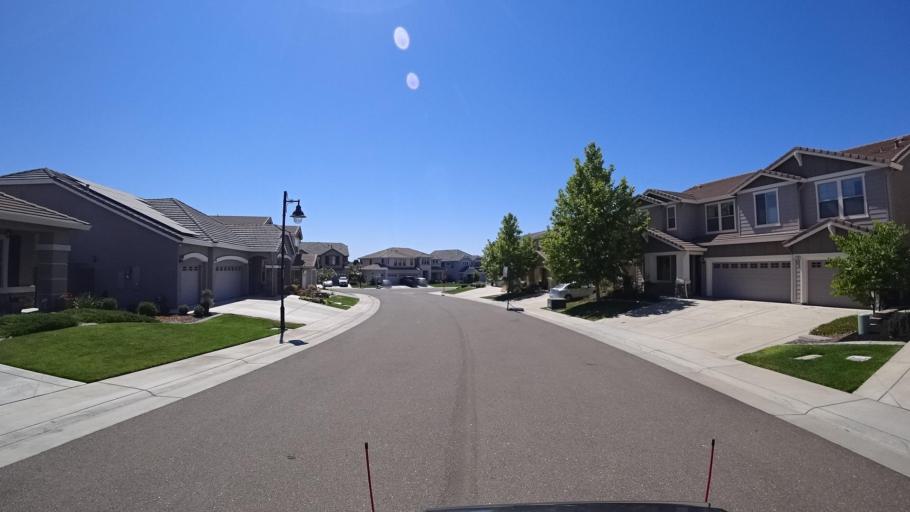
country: US
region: California
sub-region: Placer County
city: Rocklin
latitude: 38.8247
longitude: -121.2862
